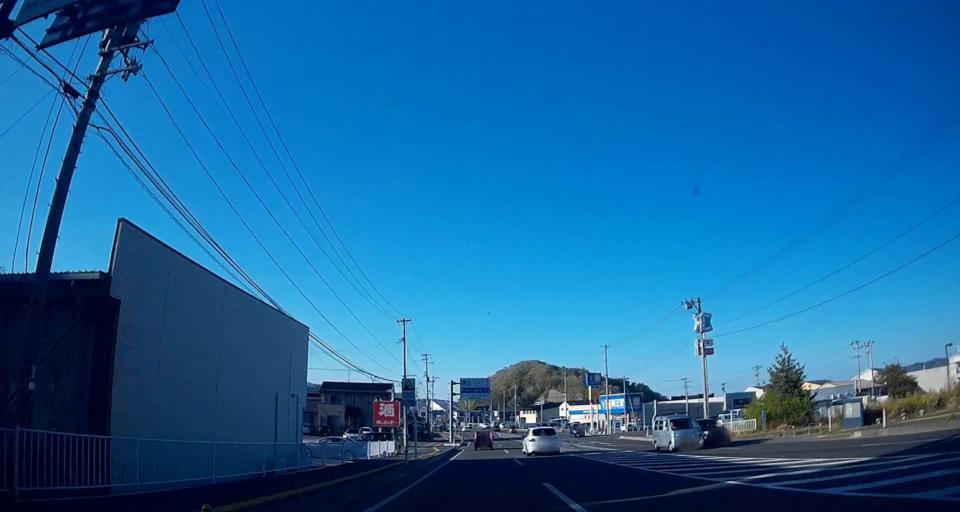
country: JP
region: Iwate
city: Miyako
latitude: 39.6201
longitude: 141.9620
